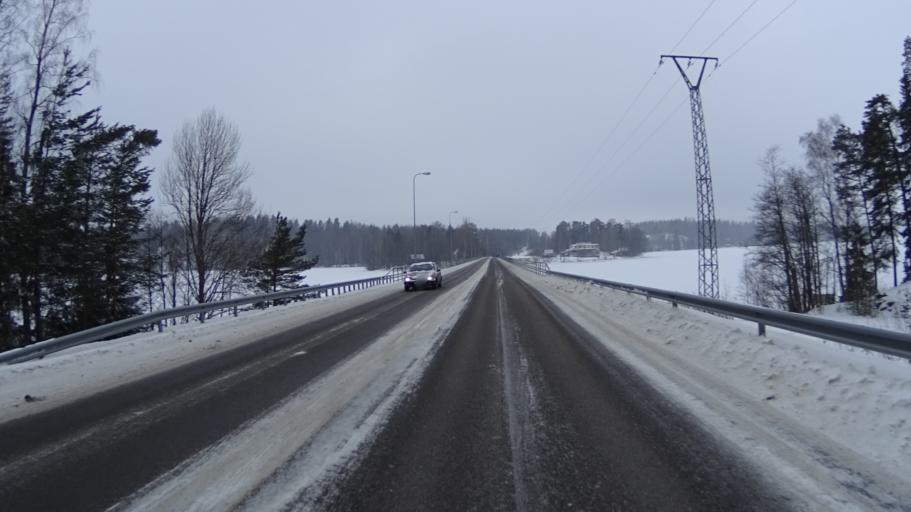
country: FI
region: Uusimaa
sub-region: Helsinki
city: Lohja
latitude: 60.3604
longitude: 24.1727
